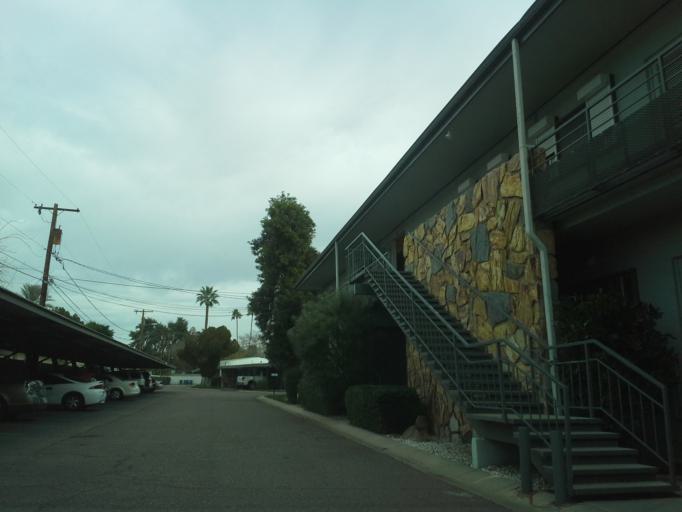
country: US
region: Arizona
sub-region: Maricopa County
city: Phoenix
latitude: 33.5315
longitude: -112.0801
